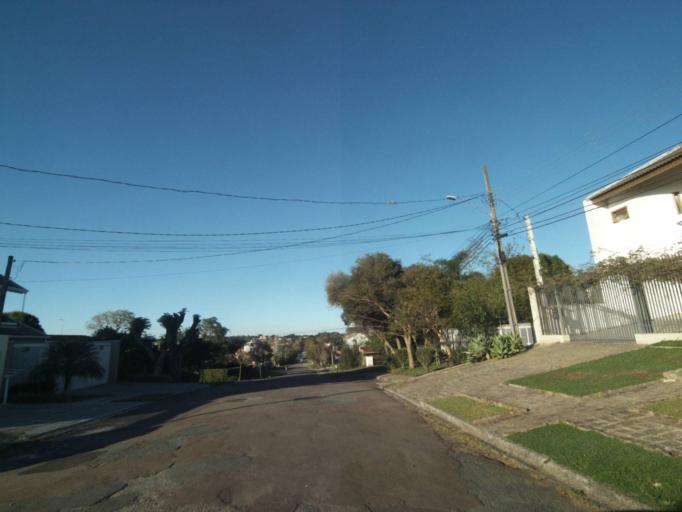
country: BR
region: Parana
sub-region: Curitiba
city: Curitiba
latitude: -25.3894
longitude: -49.2506
